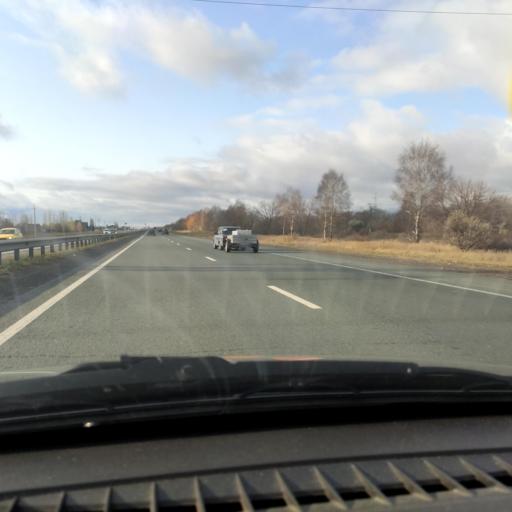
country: RU
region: Samara
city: Tol'yatti
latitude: 53.5762
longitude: 49.4328
